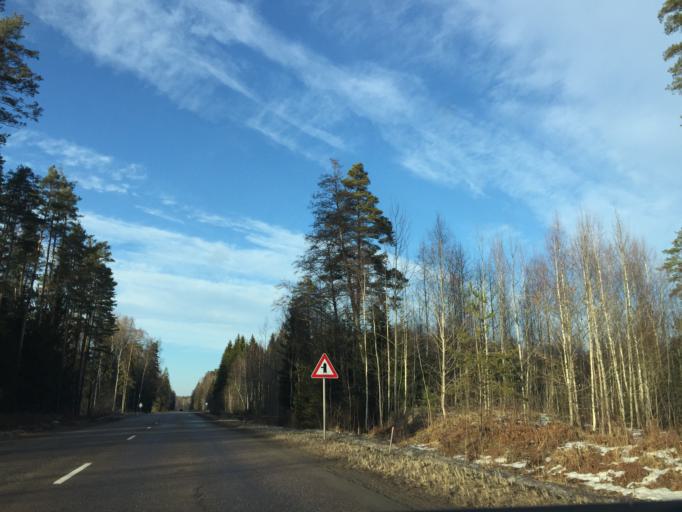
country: LV
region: Kekava
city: Balozi
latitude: 56.7399
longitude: 24.1087
